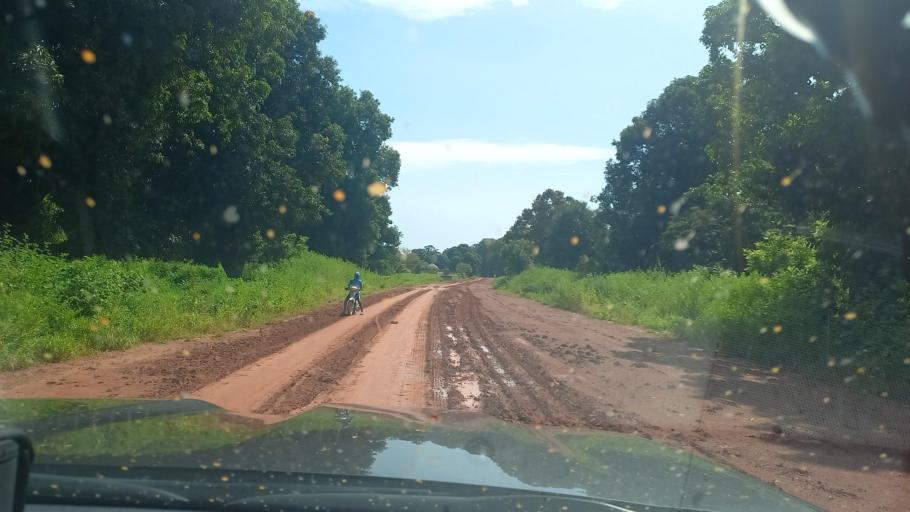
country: SN
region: Ziguinchor
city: Adeane
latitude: 12.6687
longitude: -16.0945
